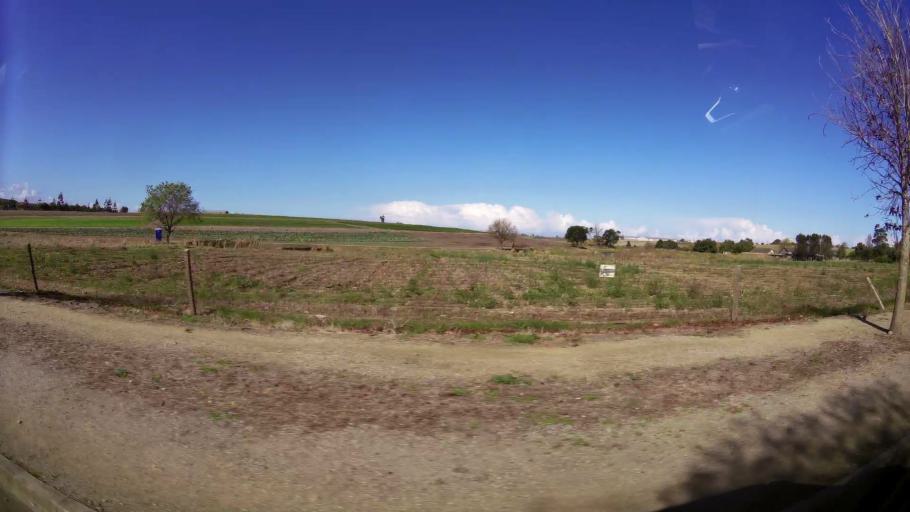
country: ZA
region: Western Cape
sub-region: Eden District Municipality
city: George
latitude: -33.9797
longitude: 22.4446
